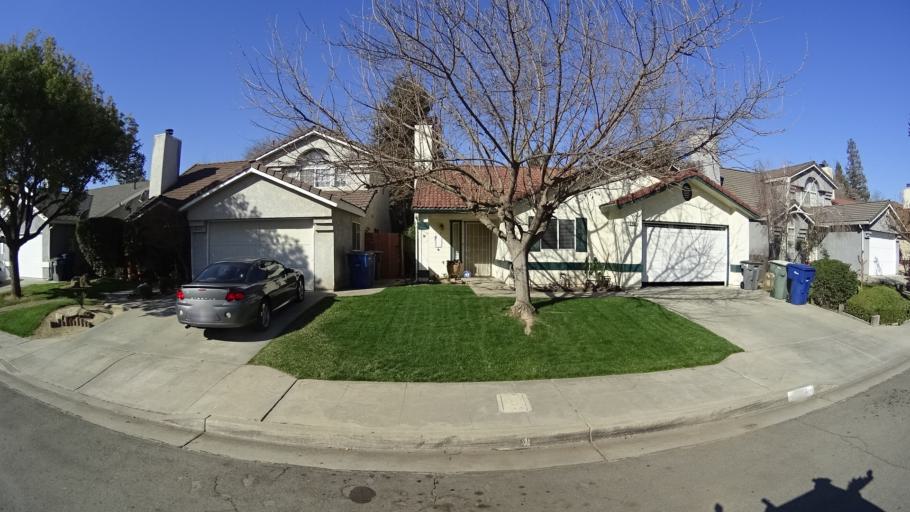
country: US
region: California
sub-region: Fresno County
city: Clovis
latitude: 36.8761
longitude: -119.7572
